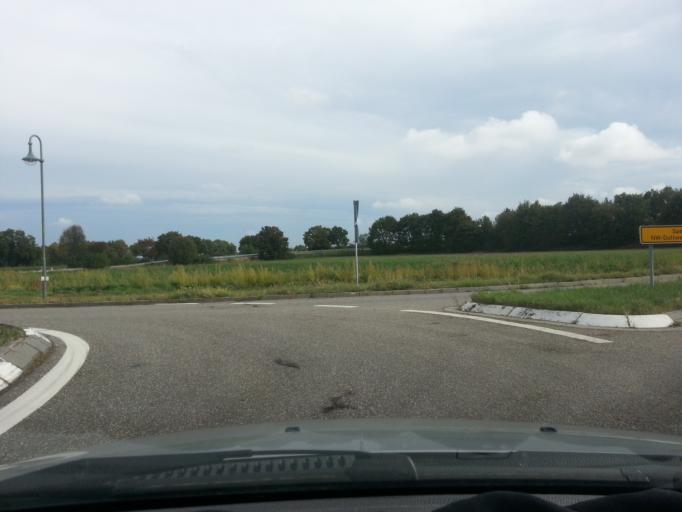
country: DE
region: Rheinland-Pfalz
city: Lachen-Speyerdorf
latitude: 49.3192
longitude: 8.2007
